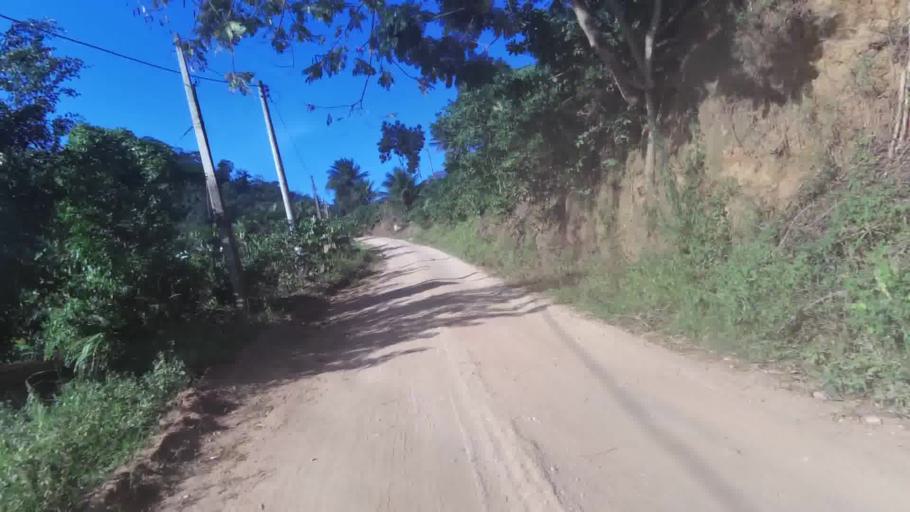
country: BR
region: Espirito Santo
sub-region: Iconha
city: Iconha
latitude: -20.7606
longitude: -40.8225
